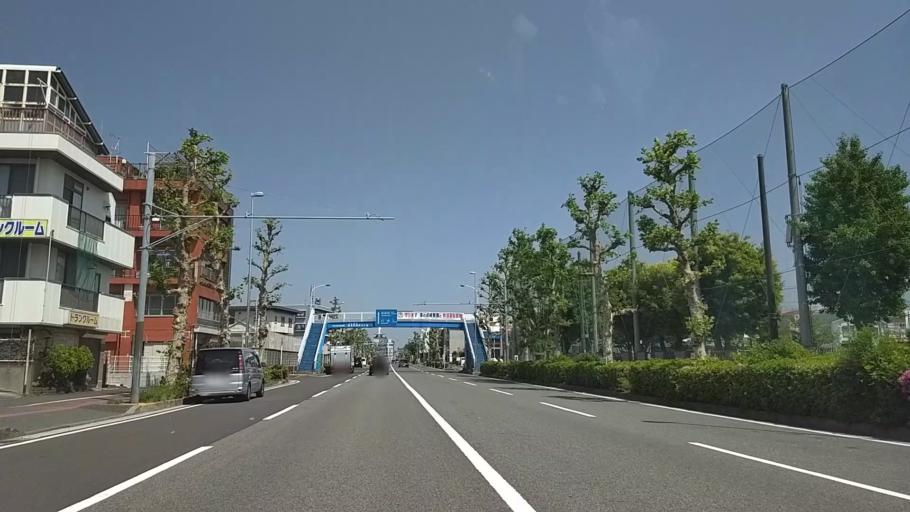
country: JP
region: Kanagawa
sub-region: Kawasaki-shi
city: Kawasaki
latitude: 35.5116
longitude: 139.6914
